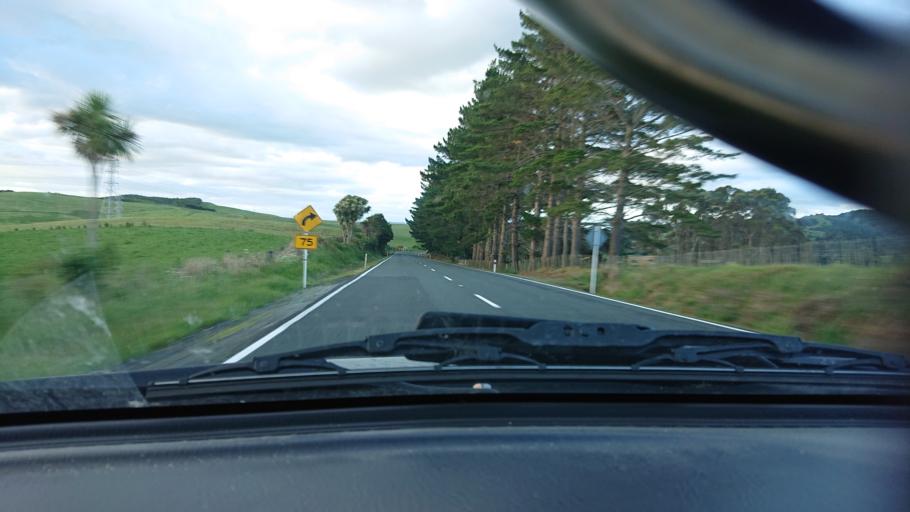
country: NZ
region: Auckland
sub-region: Auckland
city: Parakai
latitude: -36.4703
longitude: 174.4486
